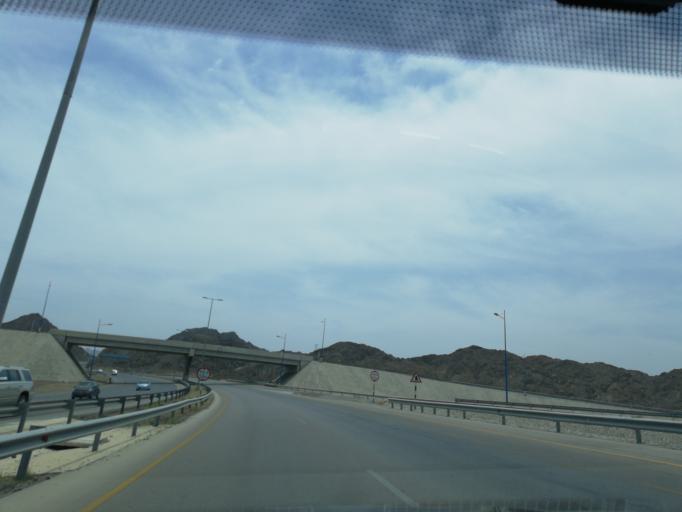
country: OM
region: Muhafazat ad Dakhiliyah
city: Izki
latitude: 22.9726
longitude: 57.7804
